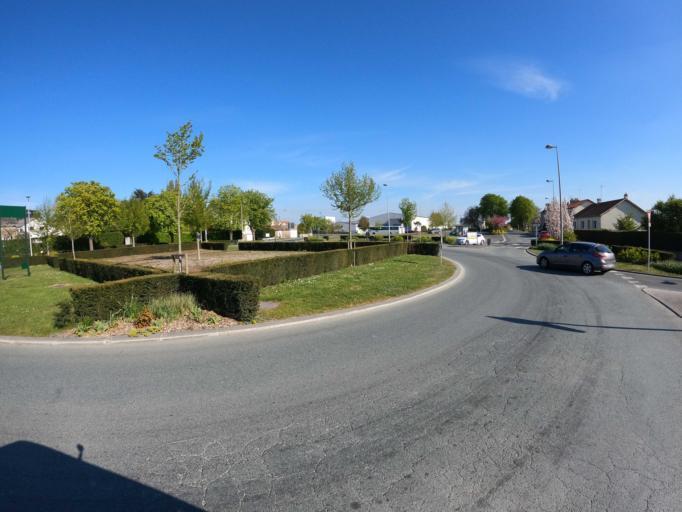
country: FR
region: Pays de la Loire
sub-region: Departement de la Vendee
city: Mortagne-sur-Sevre
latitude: 46.9962
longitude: -0.9458
